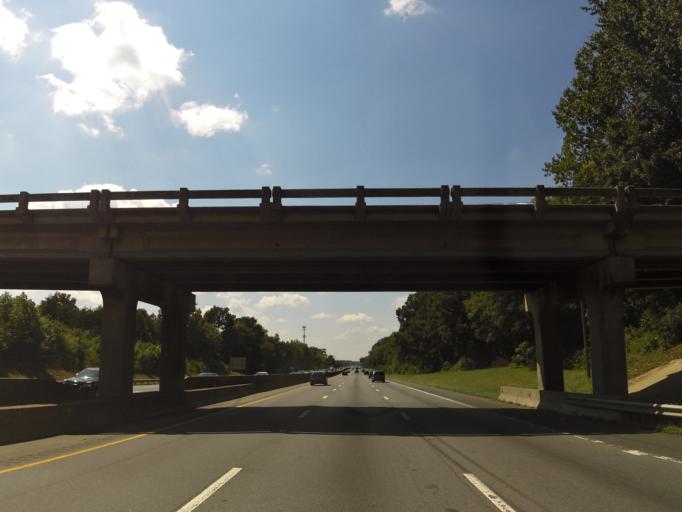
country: US
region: North Carolina
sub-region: Gaston County
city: Lowell
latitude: 35.2609
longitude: -81.1087
